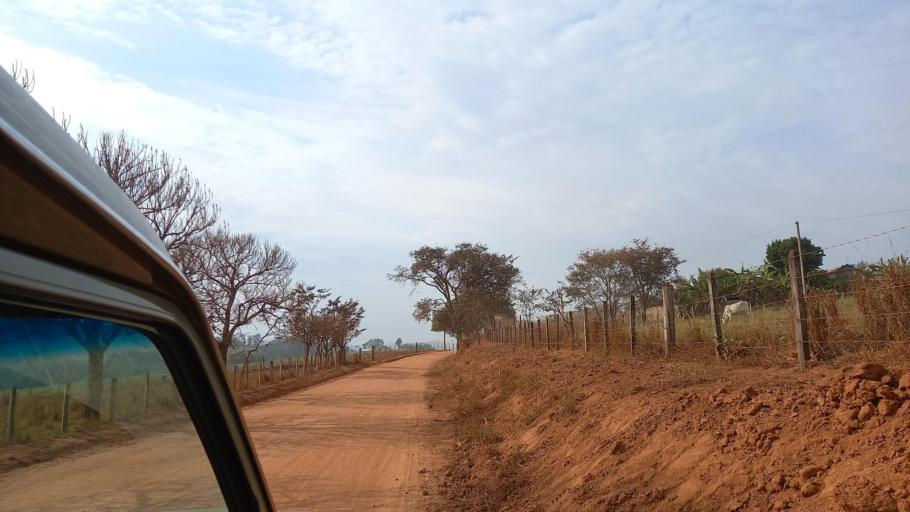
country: BR
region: Sao Paulo
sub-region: Moji-Guacu
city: Mogi-Gaucu
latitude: -22.3121
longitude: -46.8346
